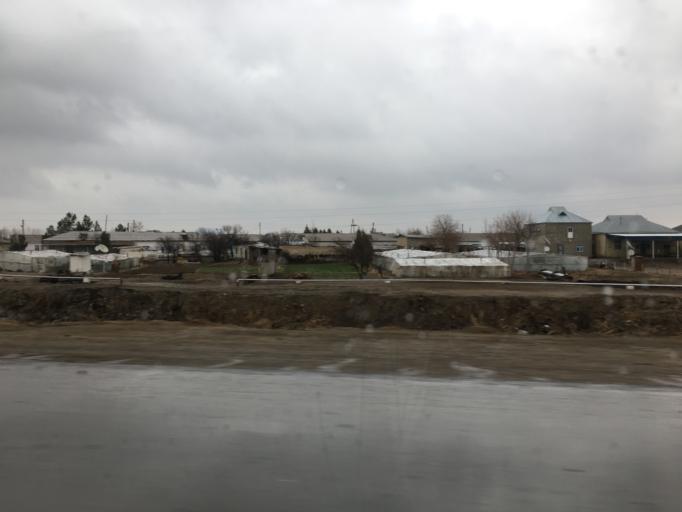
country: TM
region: Mary
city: Mary
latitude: 37.5350
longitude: 61.8871
